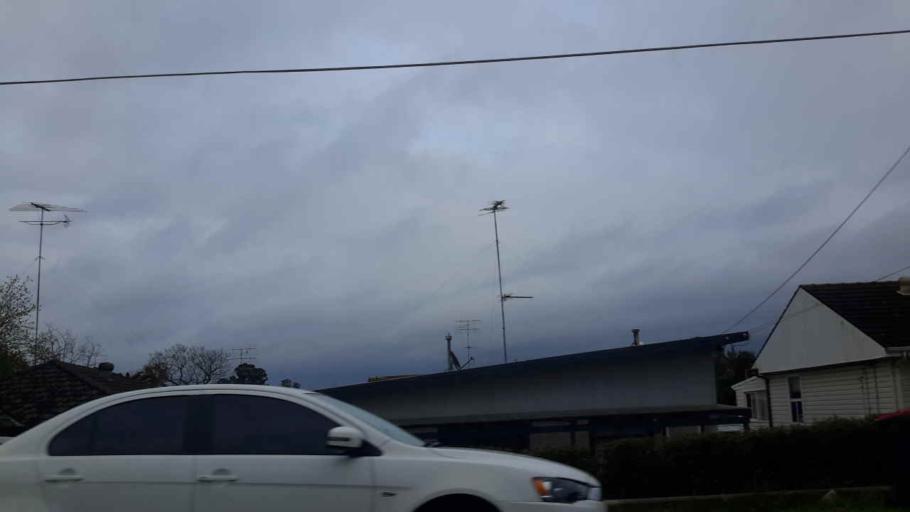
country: AU
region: New South Wales
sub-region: Penrith Municipality
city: Kingswood Park
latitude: -33.7632
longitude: 150.7099
